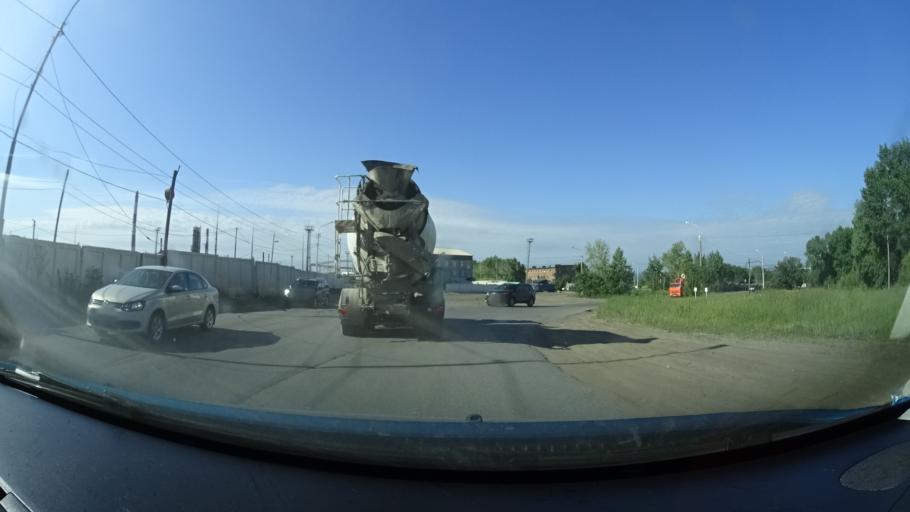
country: RU
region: Bashkortostan
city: Ufa
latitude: 54.8514
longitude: 56.0849
